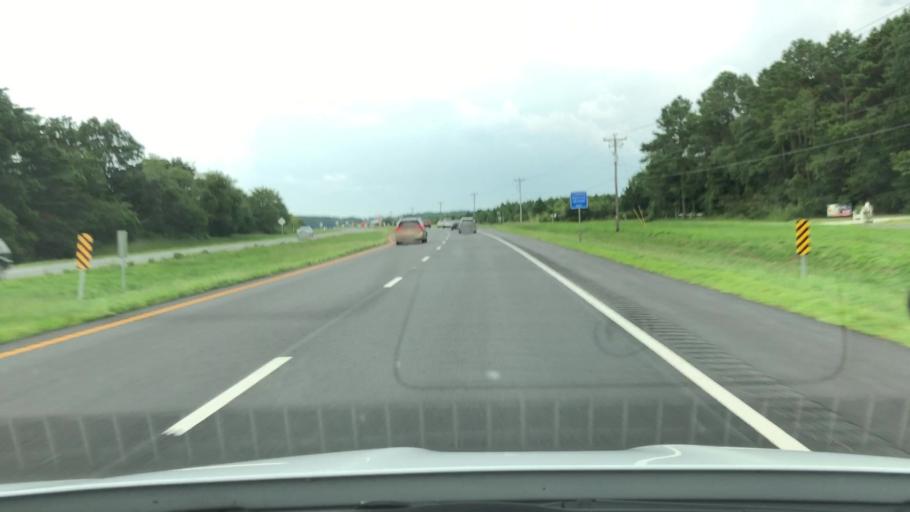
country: US
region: Virginia
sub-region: Northampton County
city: Cape Charles
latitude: 37.1483
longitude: -75.9714
